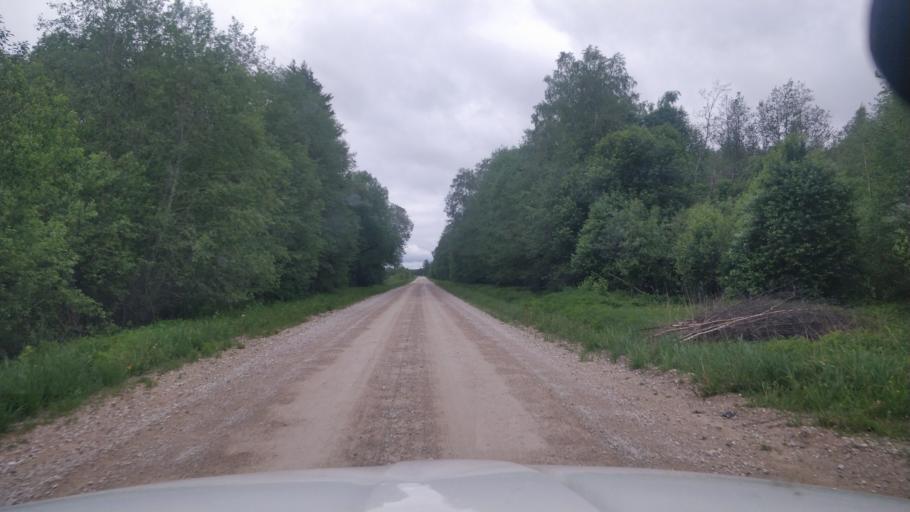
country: EE
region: Raplamaa
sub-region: Maerjamaa vald
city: Marjamaa
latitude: 58.7617
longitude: 24.2478
